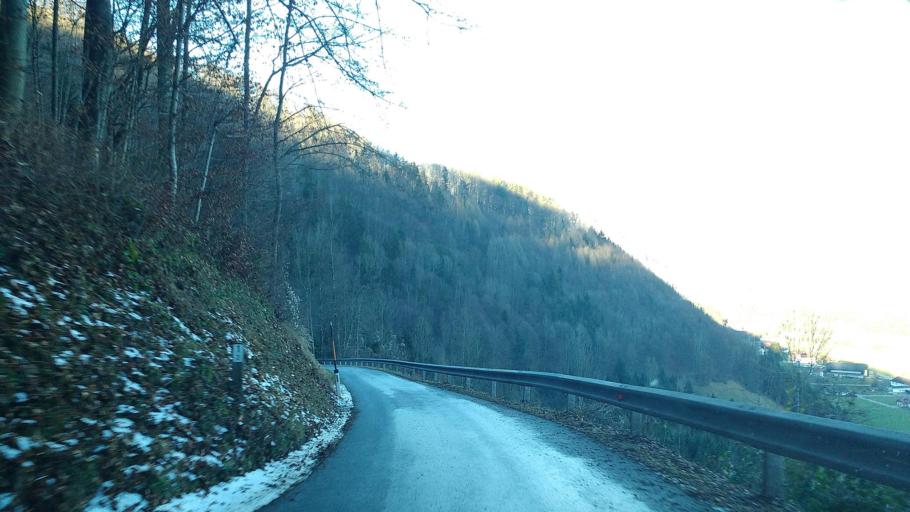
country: AT
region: Upper Austria
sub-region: Politischer Bezirk Kirchdorf an der Krems
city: Gruenburg
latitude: 47.8956
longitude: 14.2227
